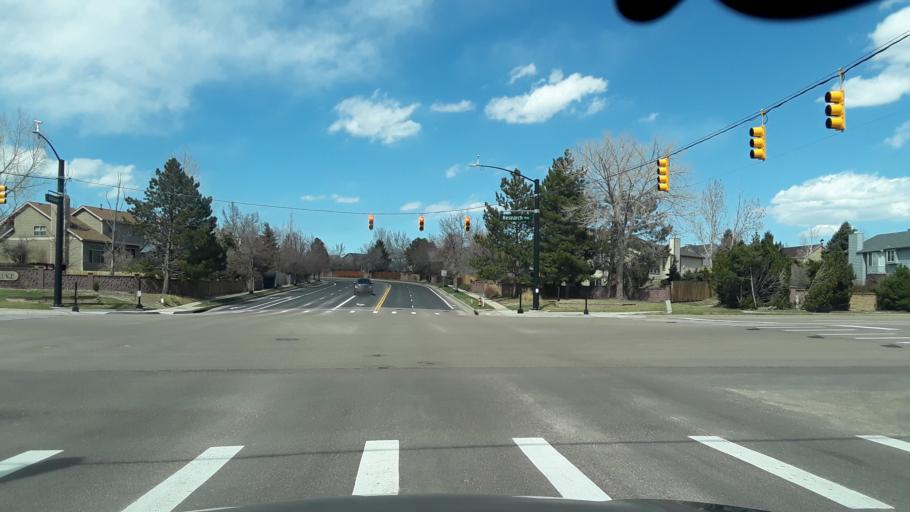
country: US
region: Colorado
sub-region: El Paso County
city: Black Forest
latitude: 38.9564
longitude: -104.7504
